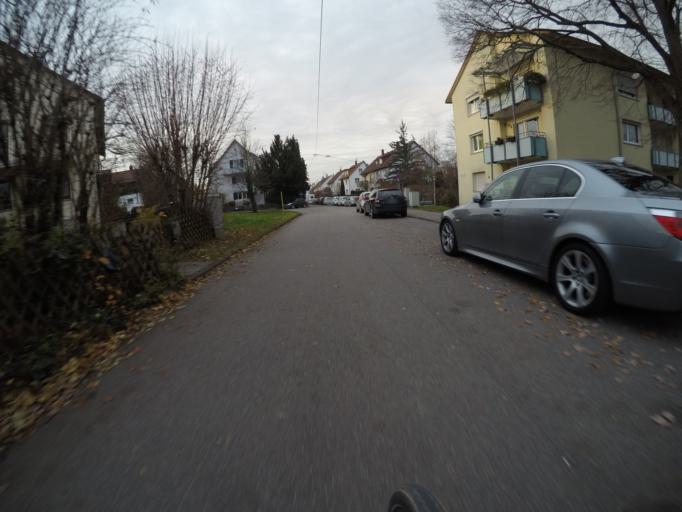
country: DE
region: Baden-Wuerttemberg
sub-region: Regierungsbezirk Stuttgart
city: Ostfildern
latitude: 48.7310
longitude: 9.2594
